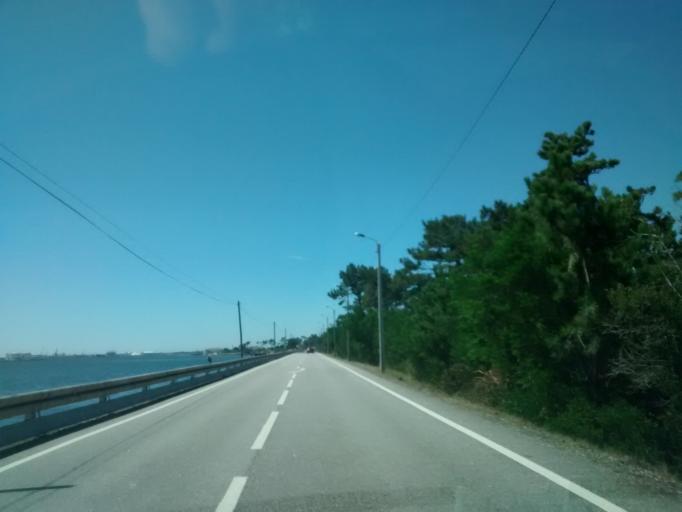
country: PT
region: Aveiro
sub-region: Ilhavo
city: Gafanha da Nazare
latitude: 40.6765
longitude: -8.7193
